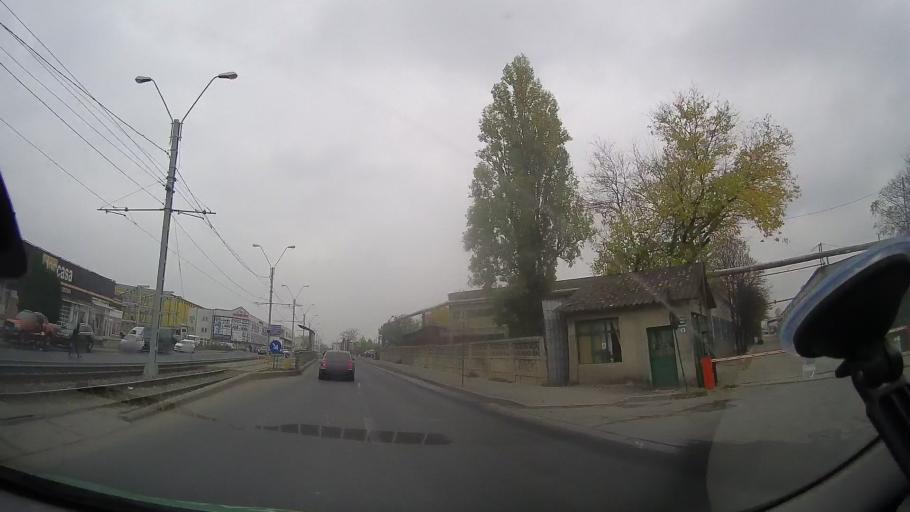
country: RO
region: Ilfov
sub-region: Comuna Chiajna
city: Rosu
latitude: 44.4278
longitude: 26.0011
